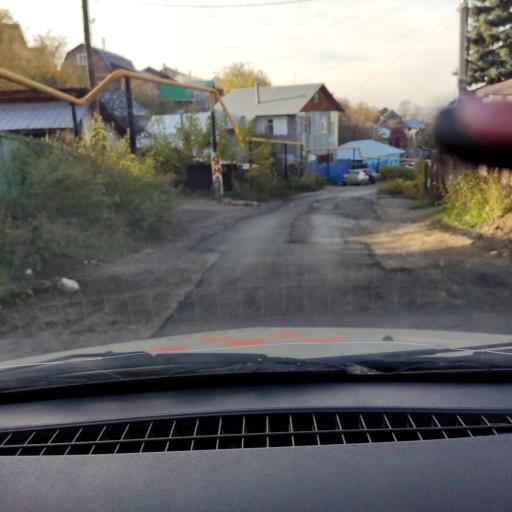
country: RU
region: Bashkortostan
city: Ufa
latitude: 54.7349
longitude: 55.9275
